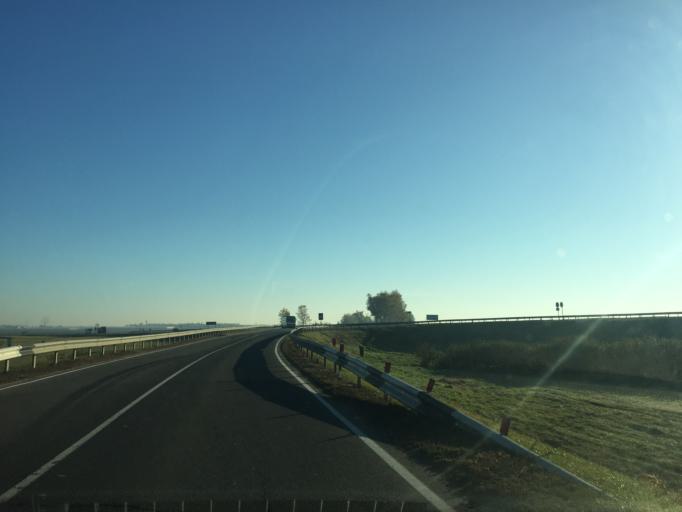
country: BY
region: Minsk
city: Pryvol'ny
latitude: 53.8169
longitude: 27.8169
